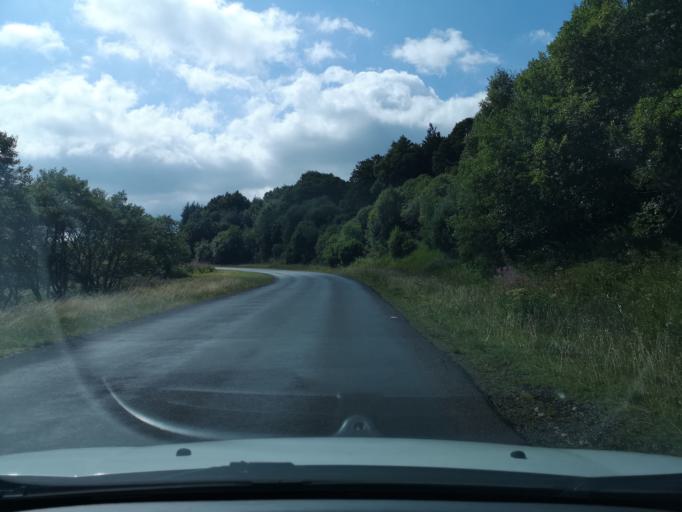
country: FR
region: Auvergne
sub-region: Departement du Puy-de-Dome
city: Mont-Dore
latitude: 45.4996
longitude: 2.8295
